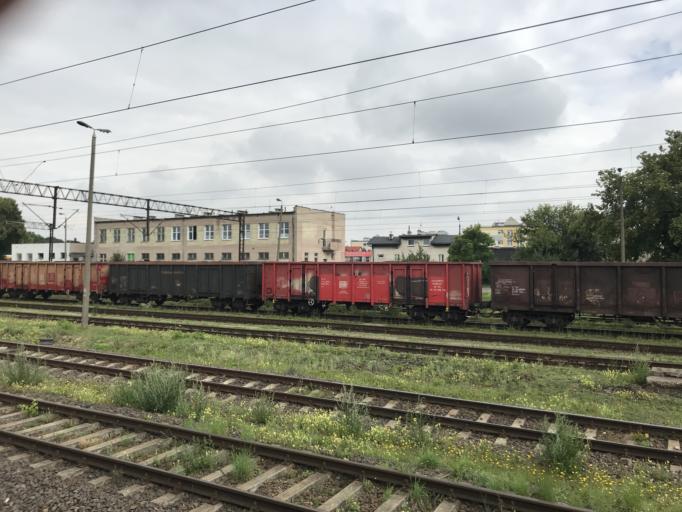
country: PL
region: Pomeranian Voivodeship
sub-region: Powiat malborski
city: Malbork
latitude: 54.0352
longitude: 19.0462
